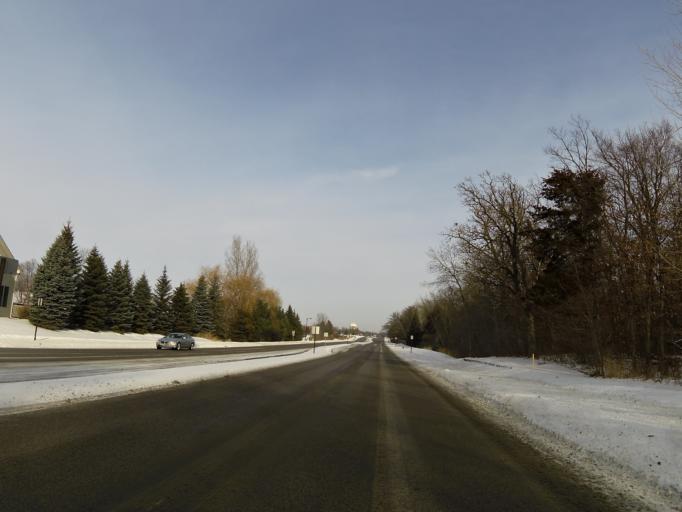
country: US
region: Minnesota
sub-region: Carver County
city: Chanhassen
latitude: 44.8556
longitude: -93.5113
